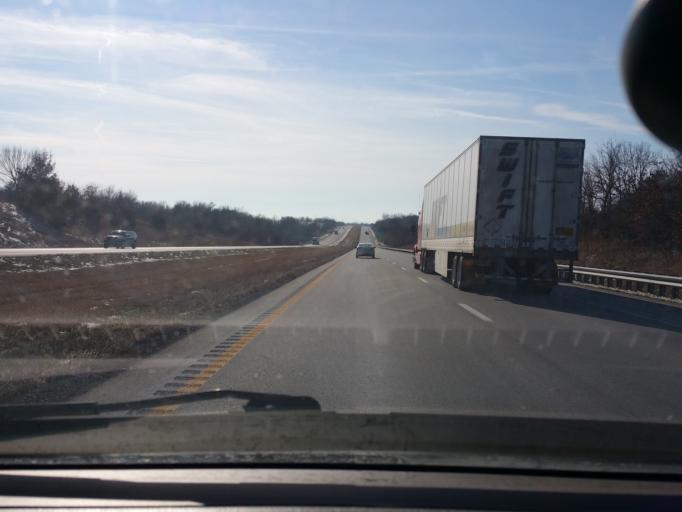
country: US
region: Missouri
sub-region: Clinton County
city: Cameron
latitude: 39.7749
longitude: -94.2118
